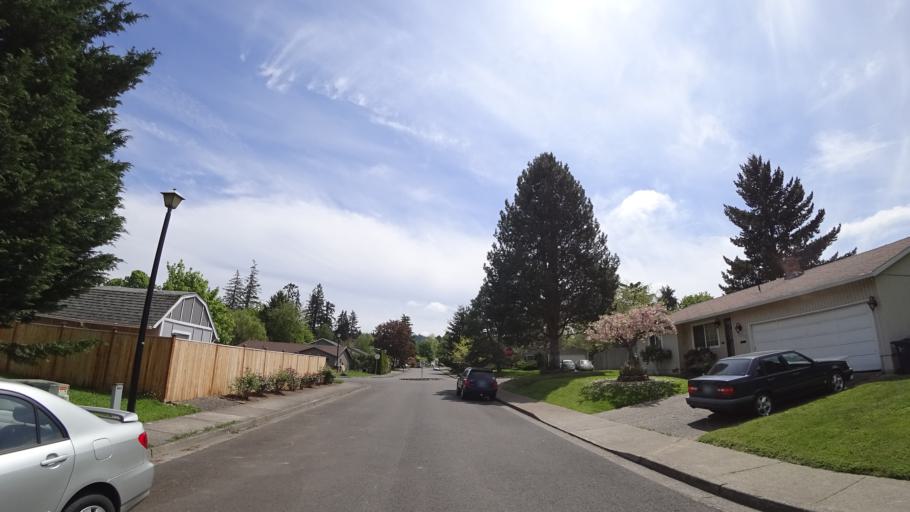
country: US
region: Oregon
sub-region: Washington County
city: Aloha
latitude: 45.4743
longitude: -122.8863
